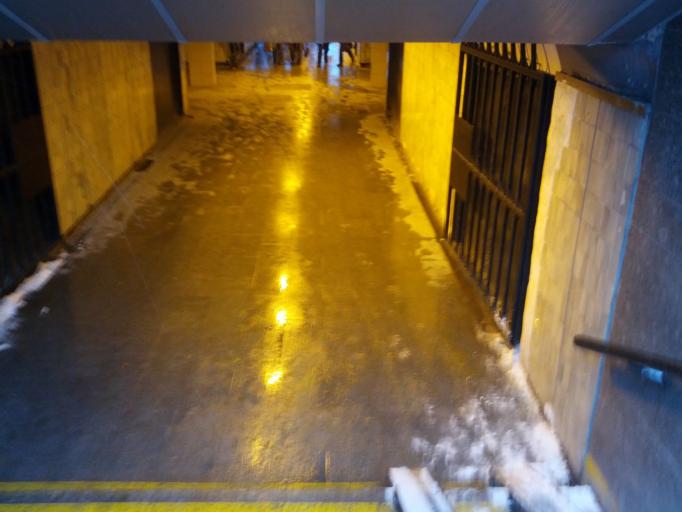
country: RU
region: St.-Petersburg
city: Kupchino
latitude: 59.8532
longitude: 30.3218
